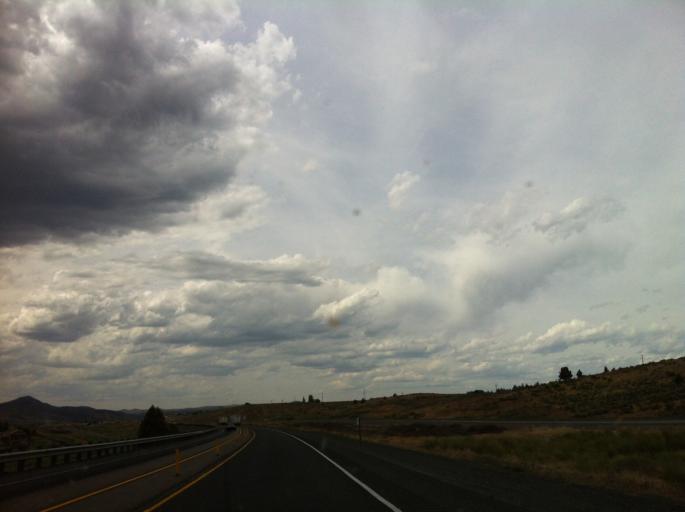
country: US
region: Oregon
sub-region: Baker County
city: Baker City
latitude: 44.5545
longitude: -117.4253
